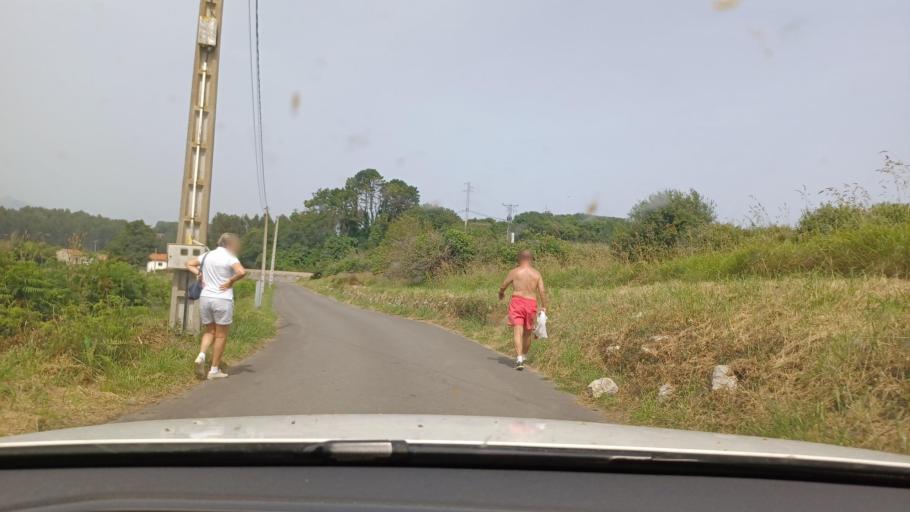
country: ES
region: Asturias
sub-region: Province of Asturias
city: Ribadesella
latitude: 43.4583
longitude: -5.0408
